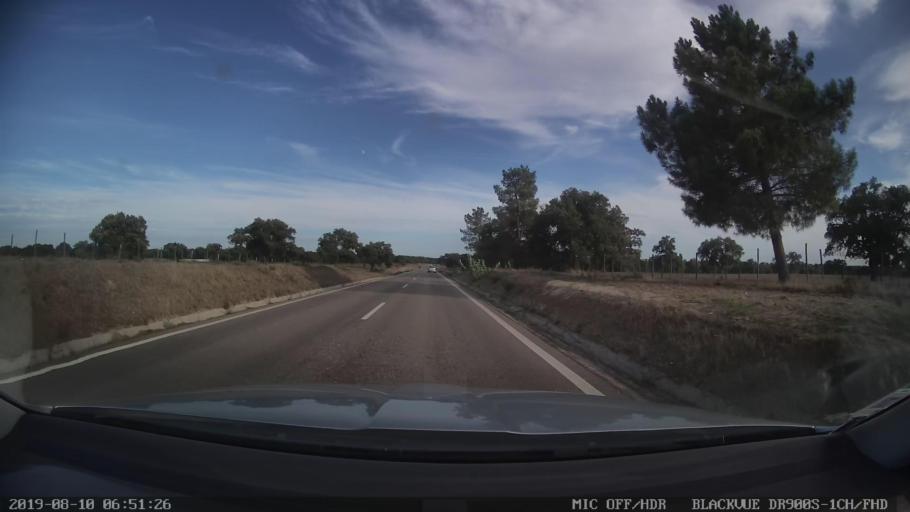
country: PT
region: Santarem
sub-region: Benavente
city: Poceirao
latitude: 38.8935
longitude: -8.7492
